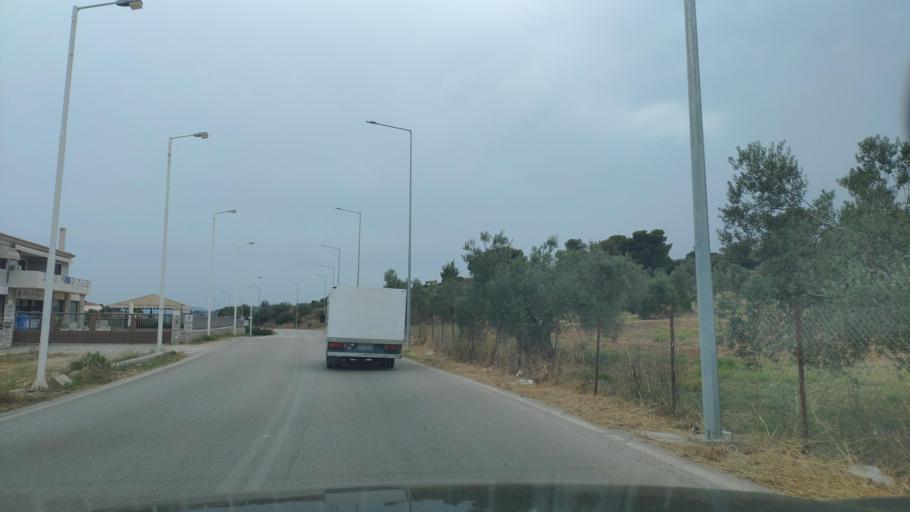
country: GR
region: Peloponnese
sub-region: Nomos Argolidos
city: Kranidi
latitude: 37.3592
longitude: 23.1613
